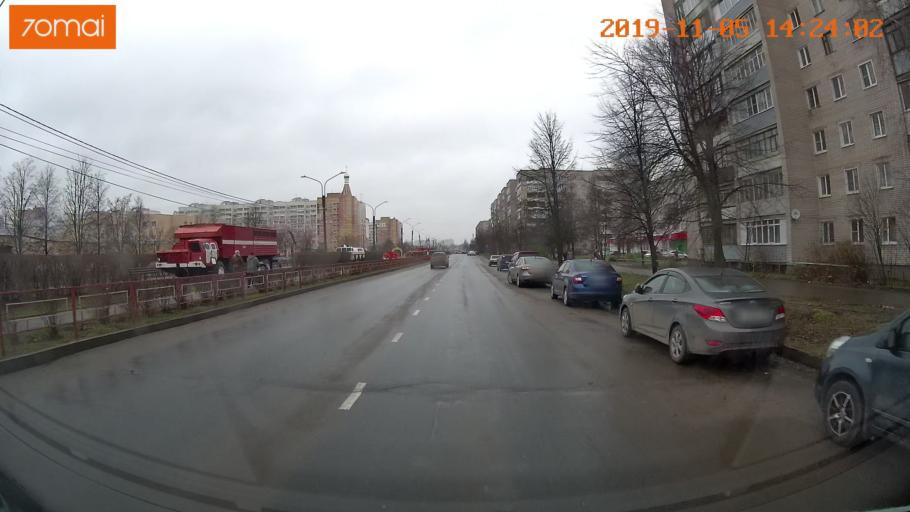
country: RU
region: Ivanovo
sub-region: Gorod Ivanovo
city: Ivanovo
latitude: 56.9664
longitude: 41.0004
